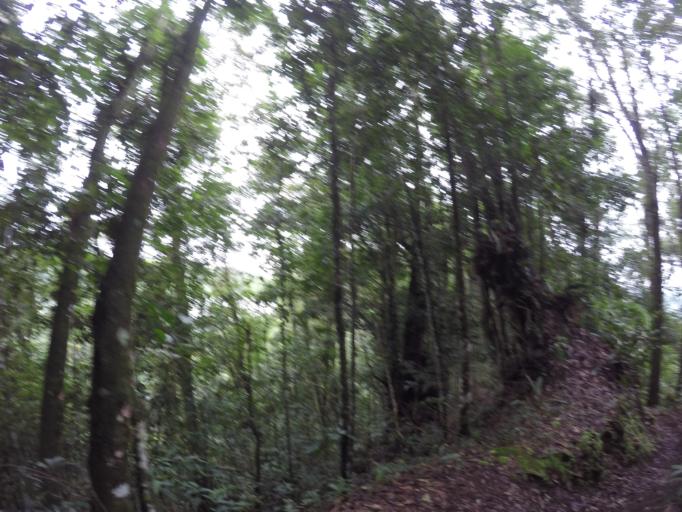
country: CO
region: Quindio
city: Filandia
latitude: 4.7107
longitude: -75.6731
